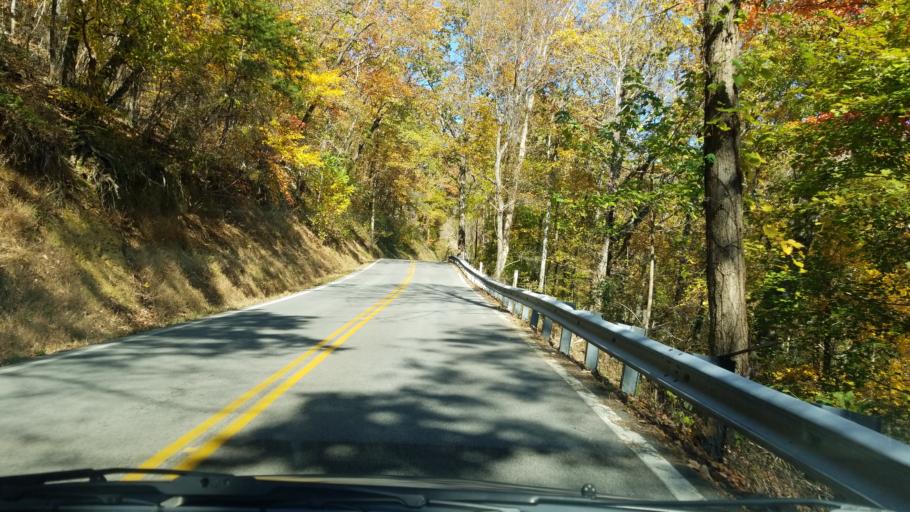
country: US
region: Tennessee
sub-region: Hamilton County
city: Falling Water
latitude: 35.2105
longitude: -85.2608
